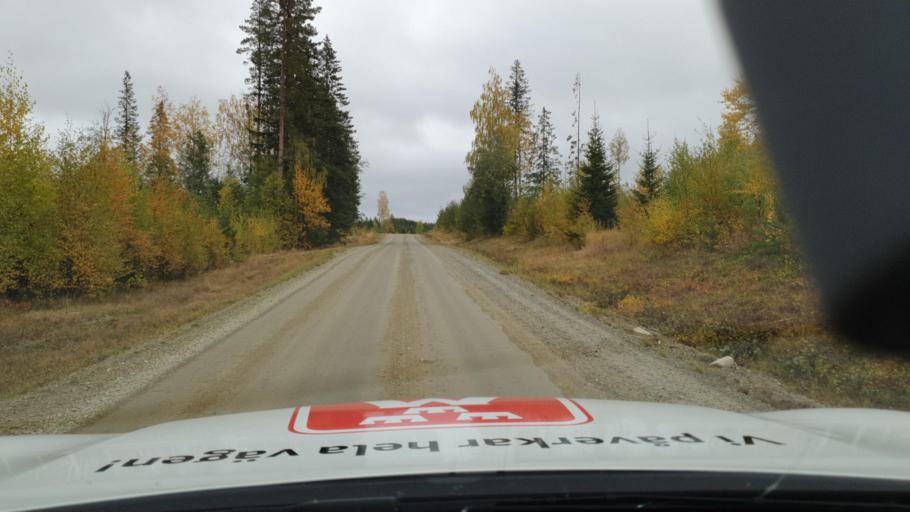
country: SE
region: Vaesterbotten
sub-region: Lycksele Kommun
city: Lycksele
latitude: 64.5795
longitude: 19.0602
